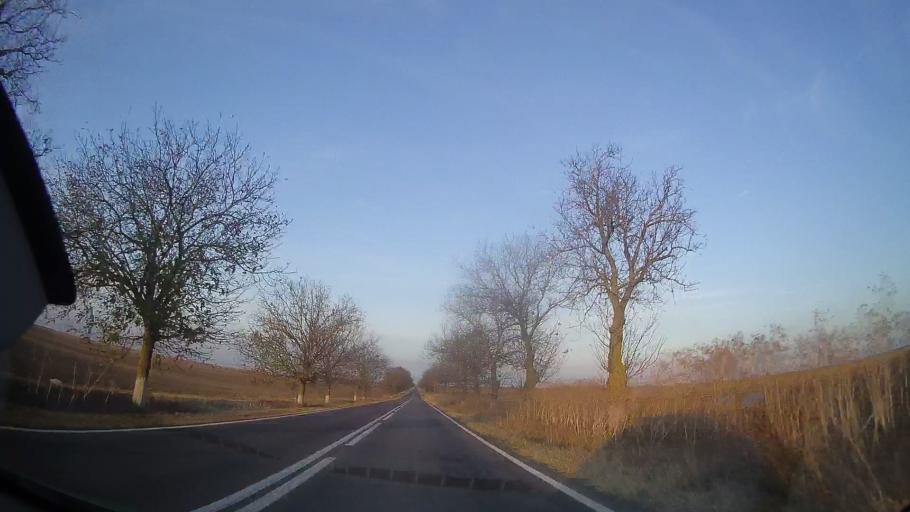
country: RO
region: Constanta
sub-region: Comuna Topraisar
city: Topraisar
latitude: 43.9878
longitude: 28.4220
